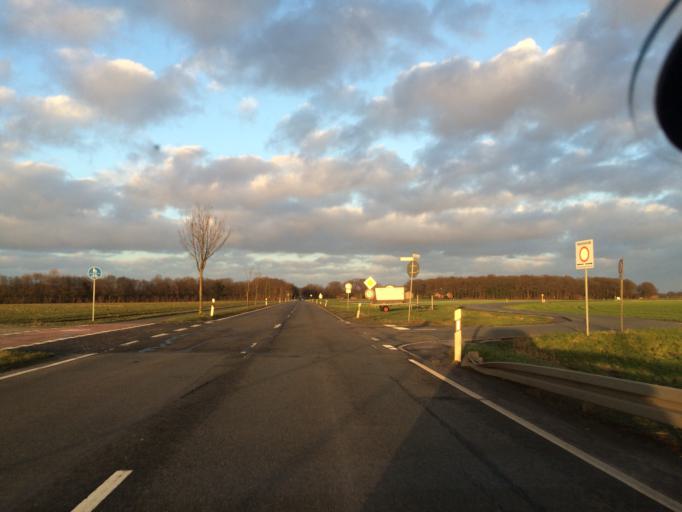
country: DE
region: North Rhine-Westphalia
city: Dorsten
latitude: 51.6779
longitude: 6.9849
